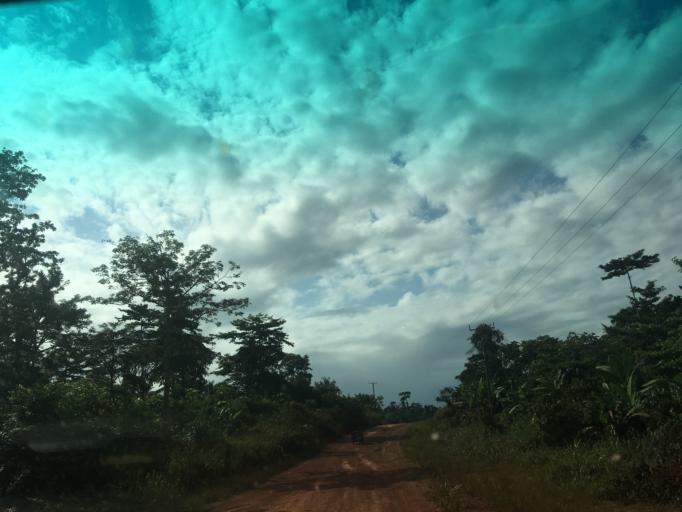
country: GH
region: Western
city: Wassa-Akropong
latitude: 5.9137
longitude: -2.4052
